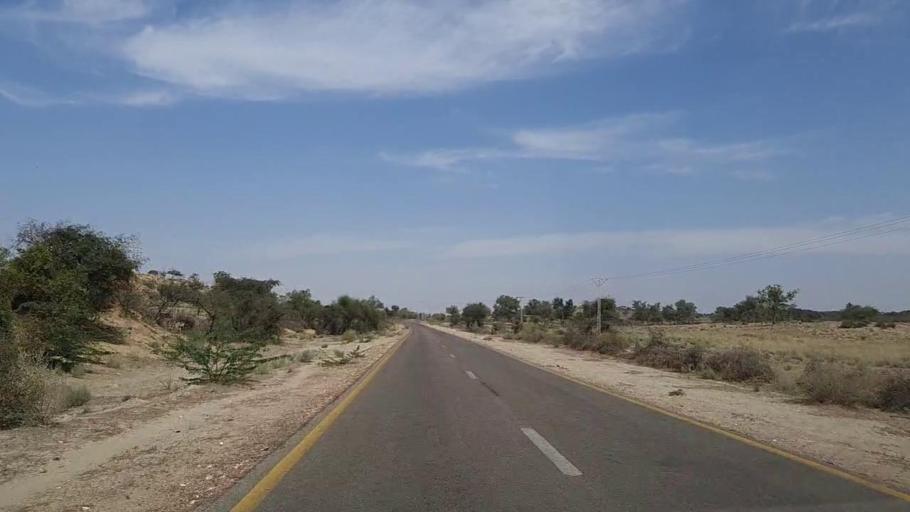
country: PK
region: Sindh
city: Mithi
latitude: 24.7921
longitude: 69.8141
